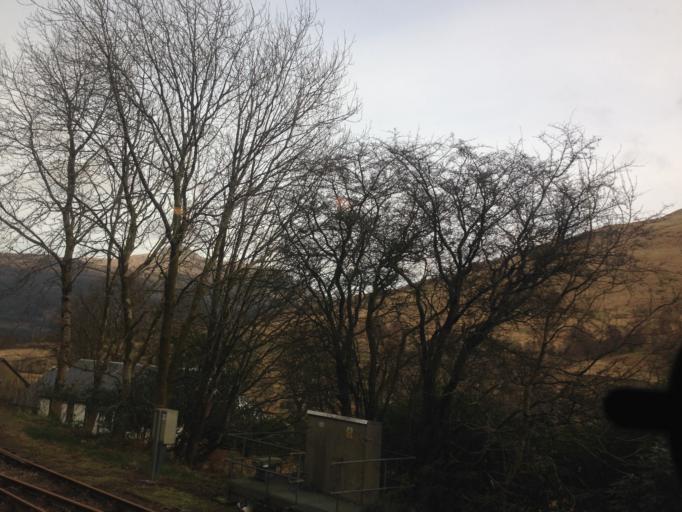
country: GB
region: Scotland
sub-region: Argyll and Bute
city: Garelochhead
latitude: 56.2021
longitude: -4.7261
